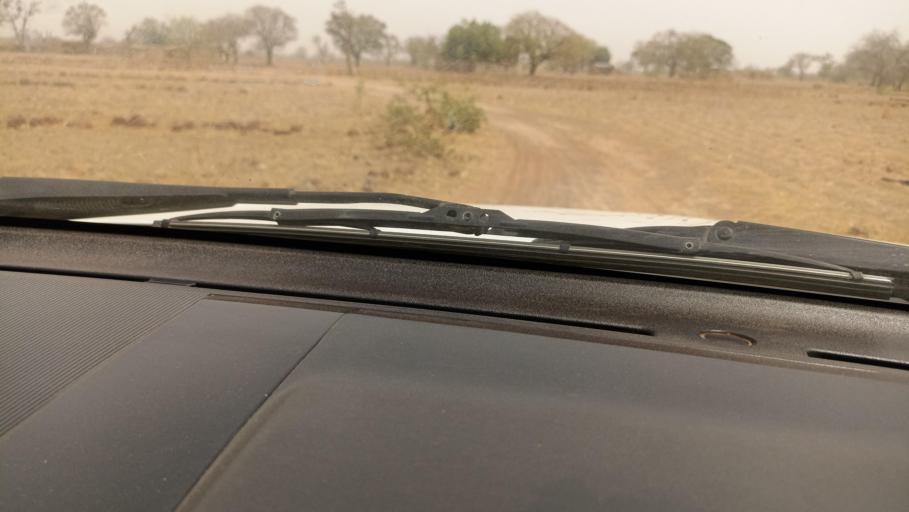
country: BF
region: Boucle du Mouhoun
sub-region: Province du Nayala
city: Toma
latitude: 12.8543
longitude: -2.7961
